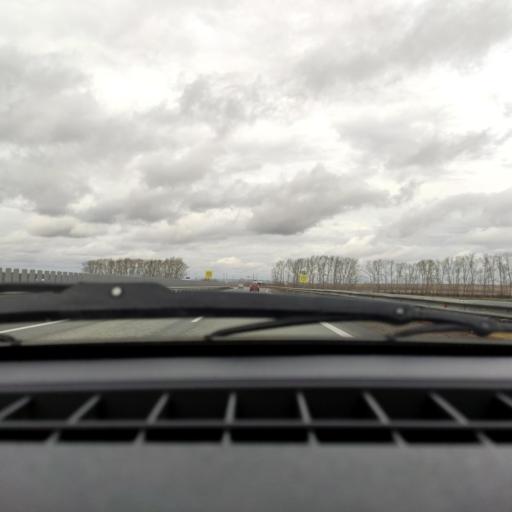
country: RU
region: Bashkortostan
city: Asanovo
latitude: 54.9558
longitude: 55.5852
